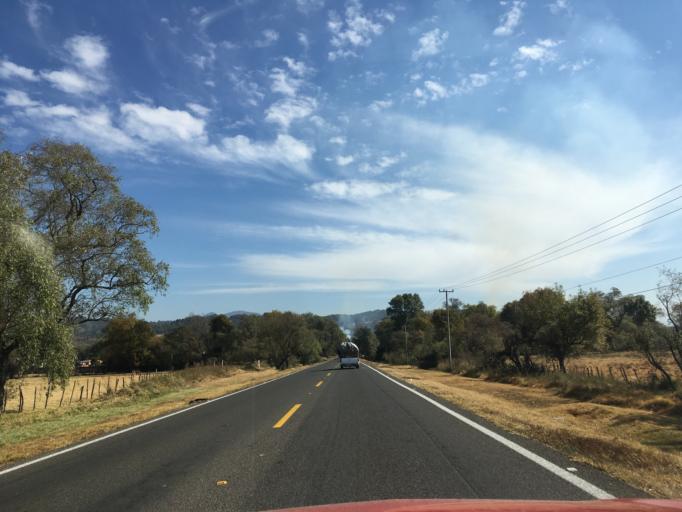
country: MX
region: Michoacan
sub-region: Hidalgo
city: Colonia Ecologica Asociacion de Lucha Social (Lucha Social)
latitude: 19.6955
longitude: -100.6133
